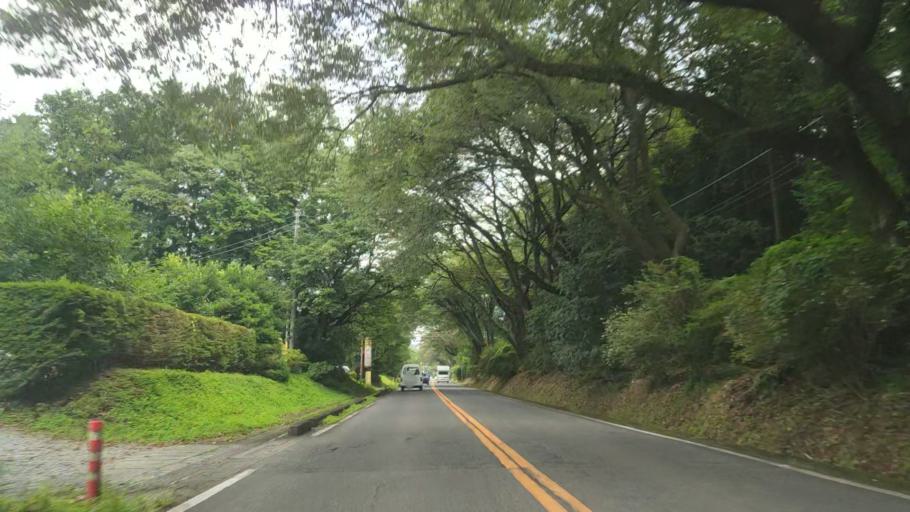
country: JP
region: Tochigi
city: Imaichi
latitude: 36.6765
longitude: 139.8010
